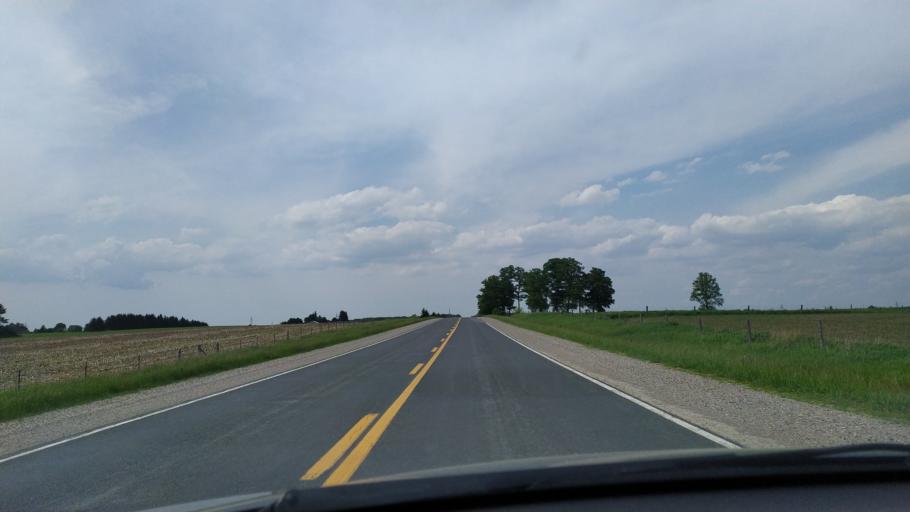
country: CA
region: Ontario
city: Ingersoll
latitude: 43.0298
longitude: -80.9727
